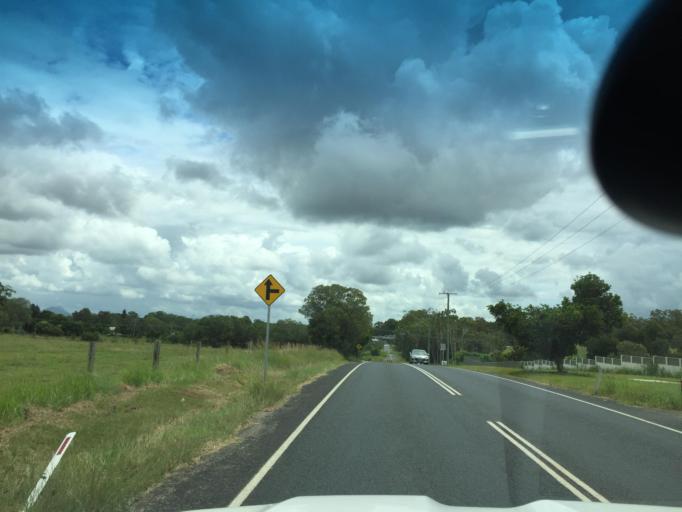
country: AU
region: Queensland
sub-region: Moreton Bay
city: Morayfield
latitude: -27.1041
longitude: 152.9695
